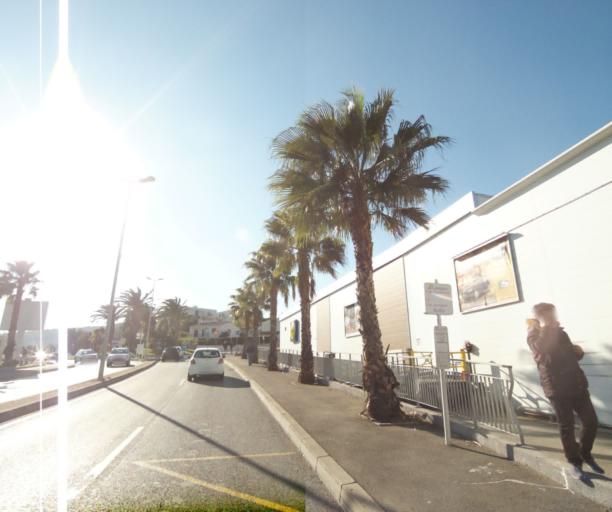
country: FR
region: Provence-Alpes-Cote d'Azur
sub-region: Departement des Bouches-du-Rhone
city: La Ciotat
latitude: 43.1893
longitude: 5.6026
